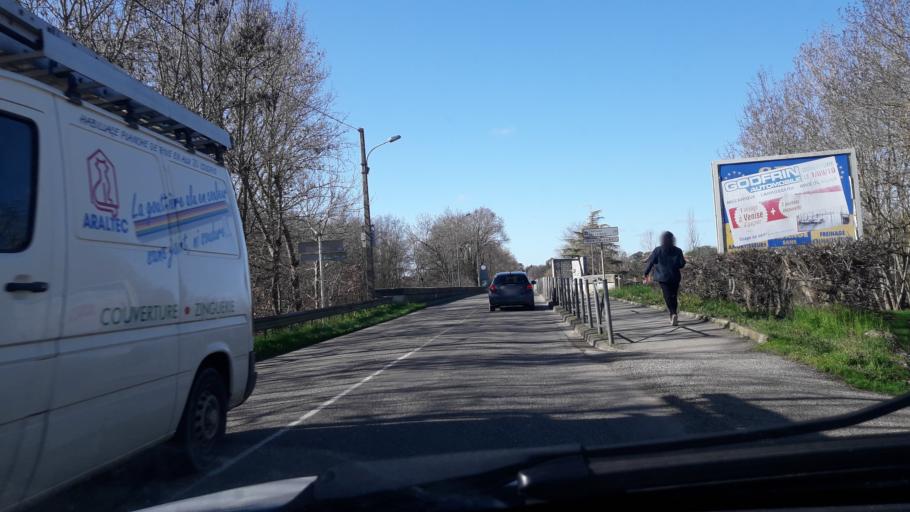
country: FR
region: Midi-Pyrenees
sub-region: Departement du Gers
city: Pujaudran
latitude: 43.6141
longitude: 1.0764
